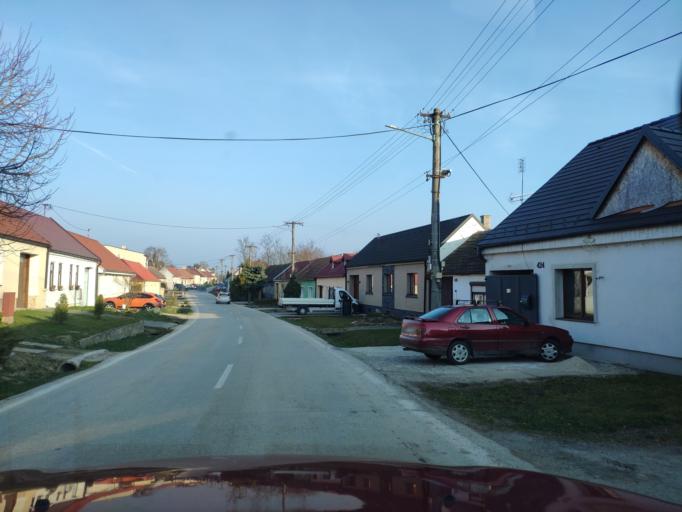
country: SK
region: Bratislavsky
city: Modra
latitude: 48.3331
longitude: 17.3999
